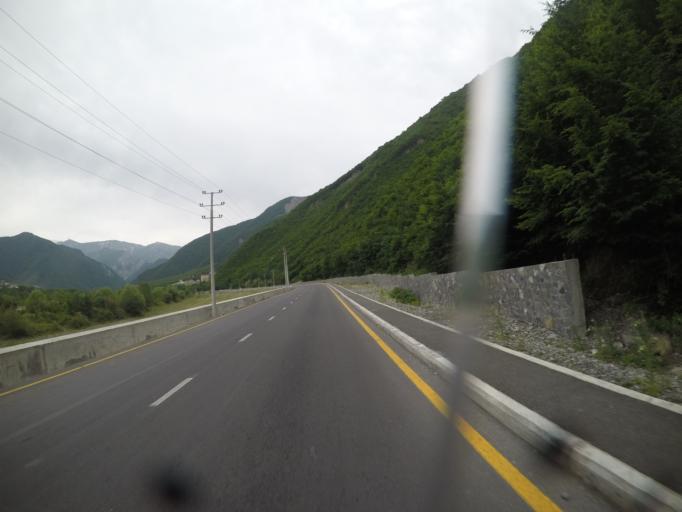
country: AZ
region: Shaki City
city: Sheki
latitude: 41.2418
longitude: 47.1909
